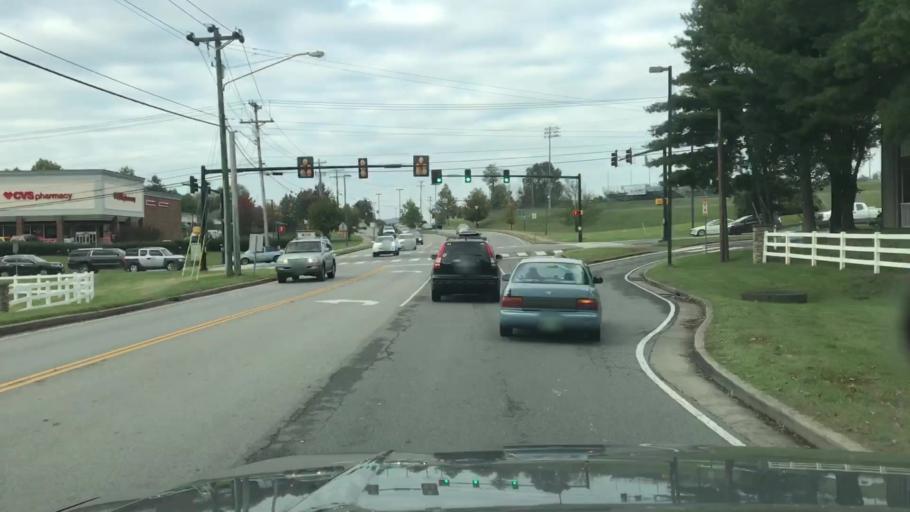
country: US
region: Tennessee
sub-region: Williamson County
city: Franklin
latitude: 35.9259
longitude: -86.8246
